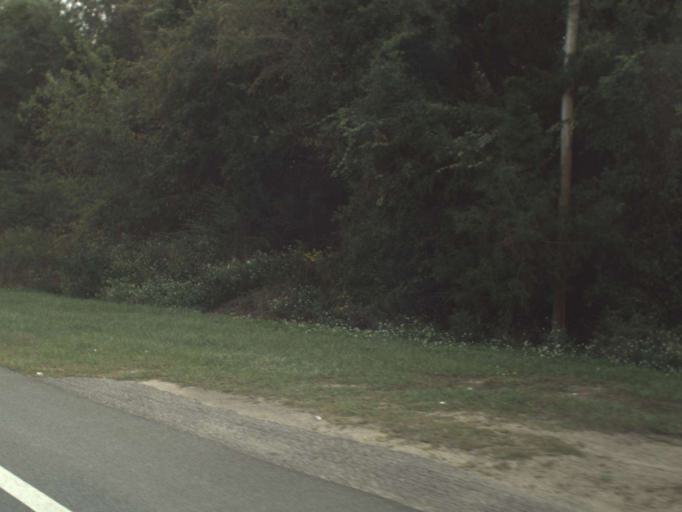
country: US
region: Florida
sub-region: Jackson County
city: Marianna
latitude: 30.6567
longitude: -85.1621
